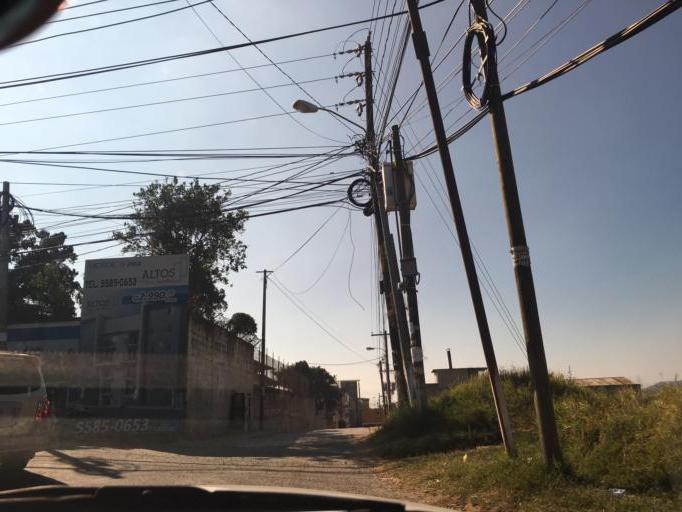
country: GT
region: Guatemala
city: Mixco
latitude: 14.6204
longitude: -90.6000
